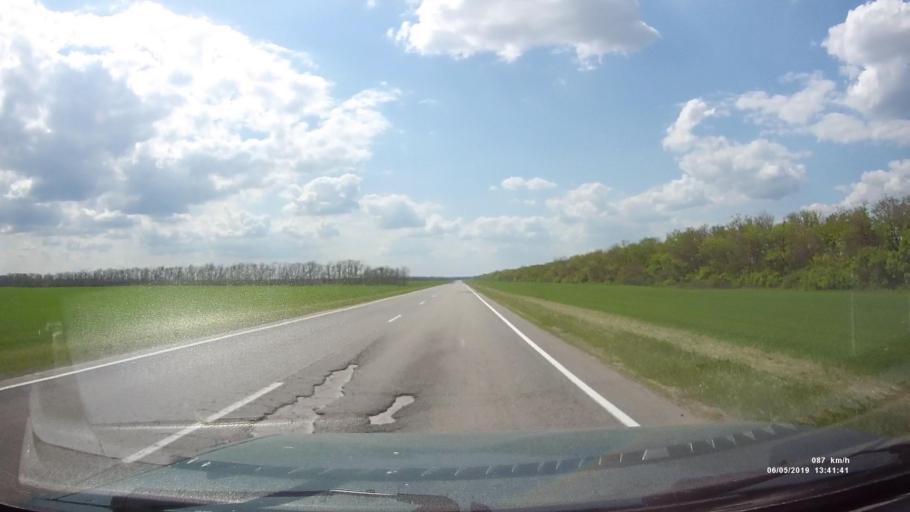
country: RU
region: Rostov
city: Semikarakorsk
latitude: 47.6624
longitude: 40.6724
